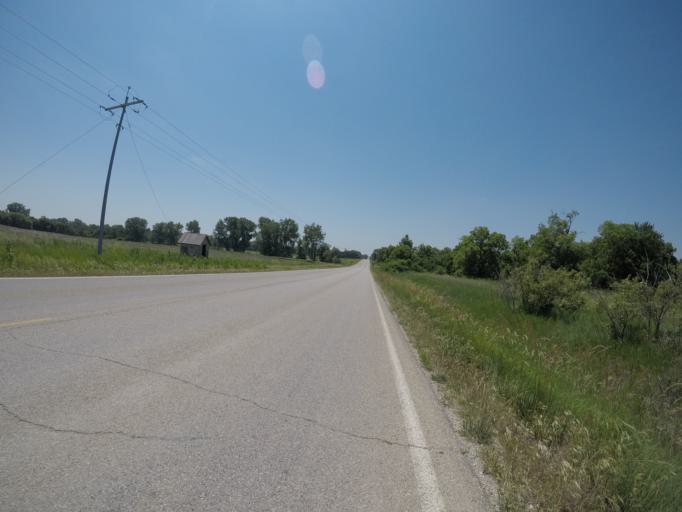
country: US
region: Kansas
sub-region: Riley County
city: Manhattan
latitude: 39.2522
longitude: -96.4451
